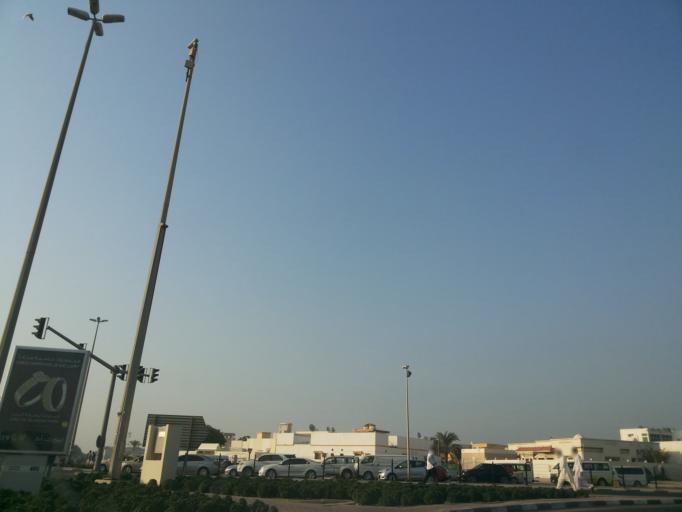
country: AE
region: Ash Shariqah
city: Sharjah
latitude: 25.2836
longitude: 55.3391
